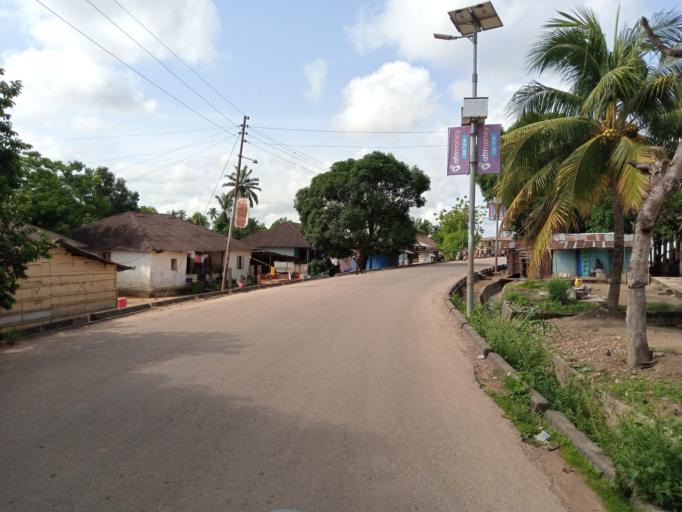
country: SL
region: Southern Province
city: Bo
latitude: 7.9723
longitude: -11.7375
